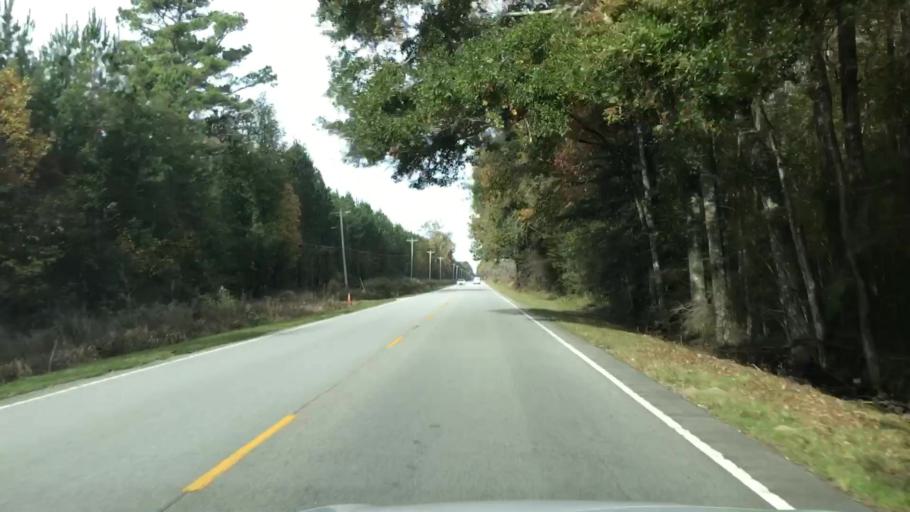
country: US
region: South Carolina
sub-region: Colleton County
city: Walterboro
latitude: 32.8048
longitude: -80.5123
